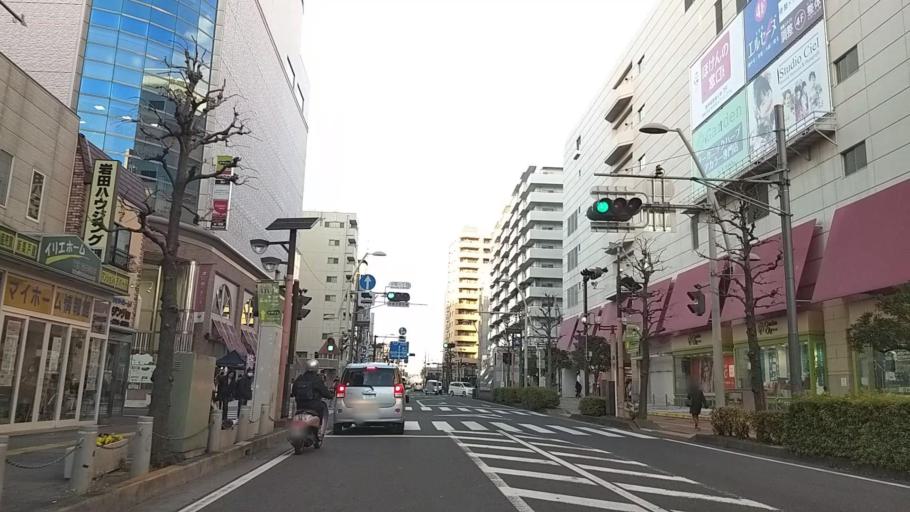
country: JP
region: Kanagawa
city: Atsugi
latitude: 35.4417
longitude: 139.3661
